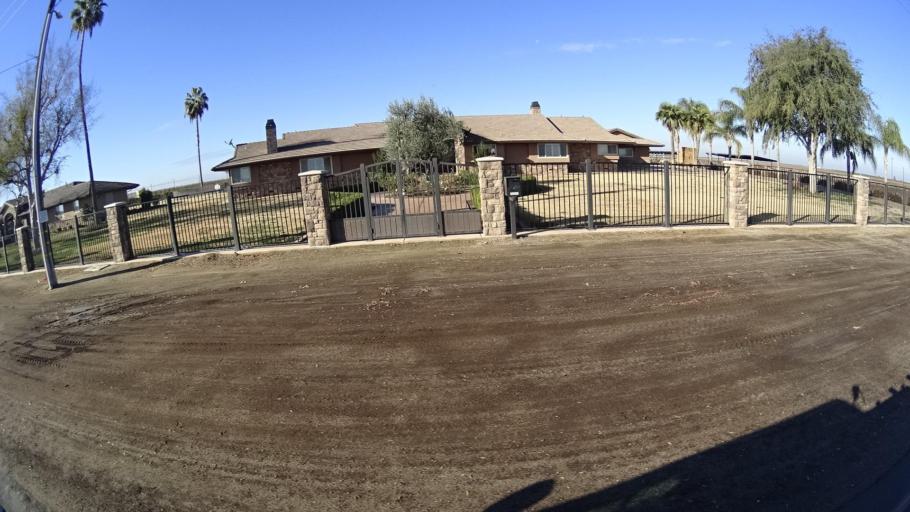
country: US
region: California
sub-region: Kern County
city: McFarland
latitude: 35.7018
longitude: -119.2759
